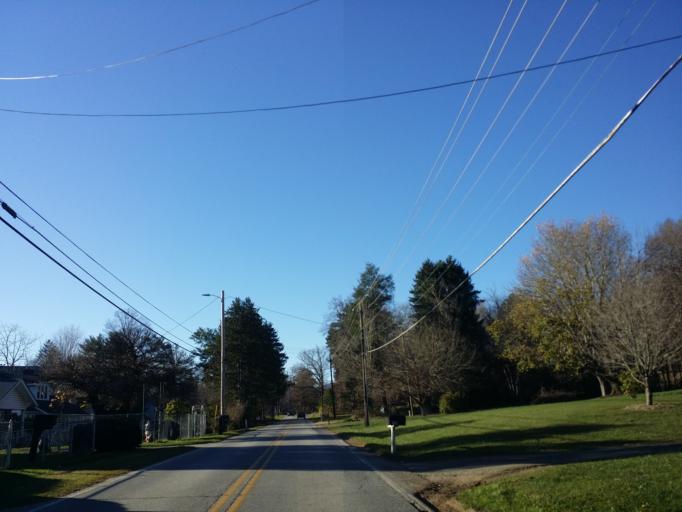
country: US
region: North Carolina
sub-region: Buncombe County
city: Swannanoa
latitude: 35.6068
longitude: -82.4108
